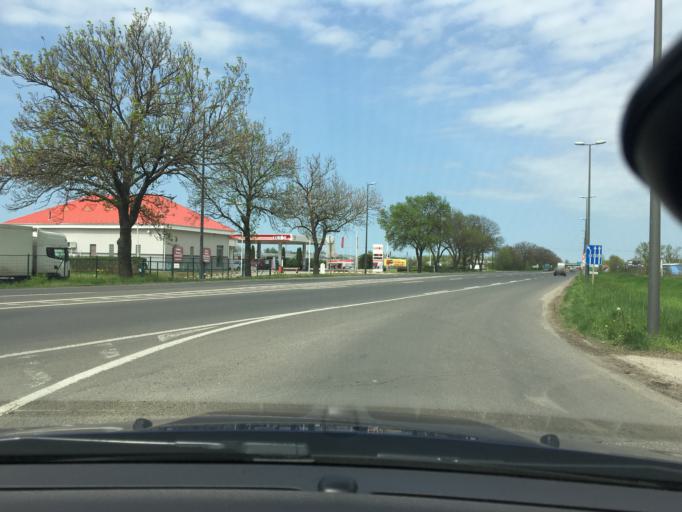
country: HU
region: Csongrad
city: Szeged
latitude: 46.2882
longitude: 20.1730
